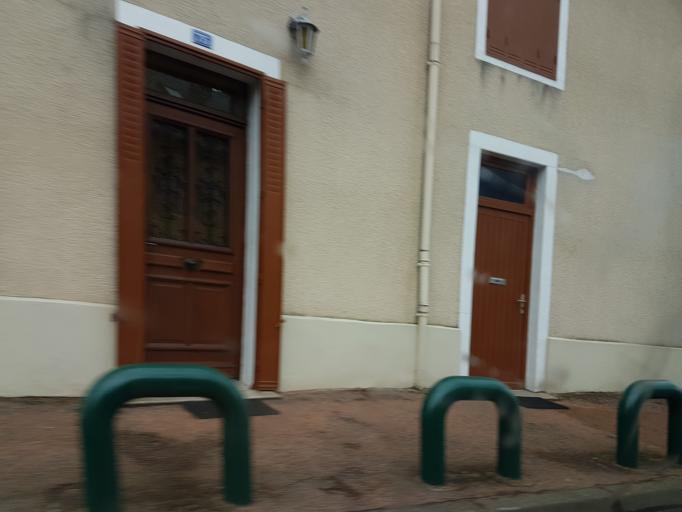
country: FR
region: Bourgogne
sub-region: Departement de la Nievre
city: Chateau-Chinon(Ville)
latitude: 47.0434
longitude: 4.0201
